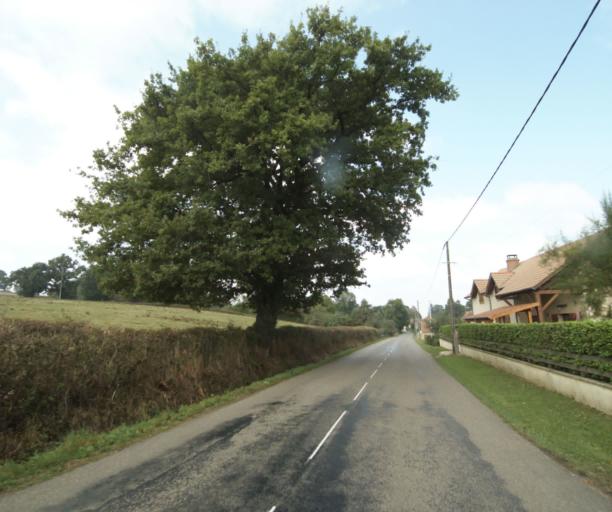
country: FR
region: Bourgogne
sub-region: Departement de Saone-et-Loire
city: Charolles
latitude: 46.4294
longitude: 4.3006
